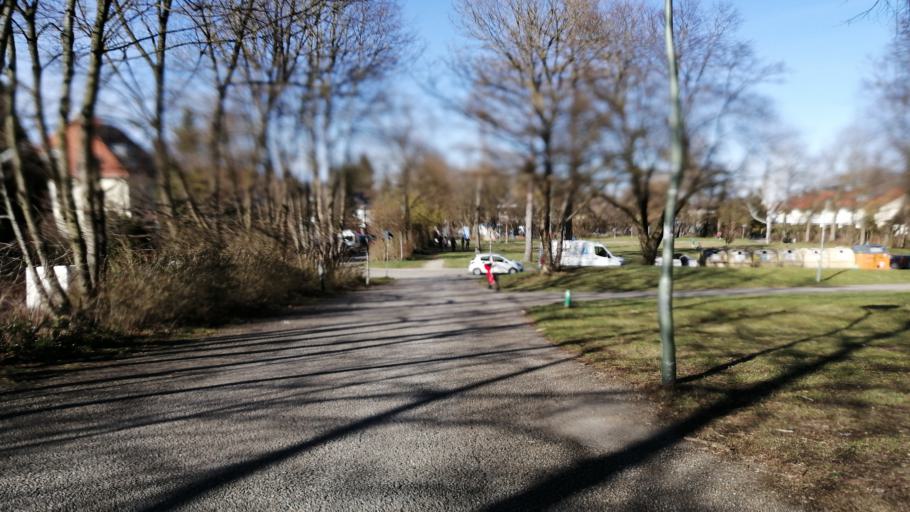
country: DE
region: Bavaria
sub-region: Upper Bavaria
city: Neuried
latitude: 48.1252
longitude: 11.5153
